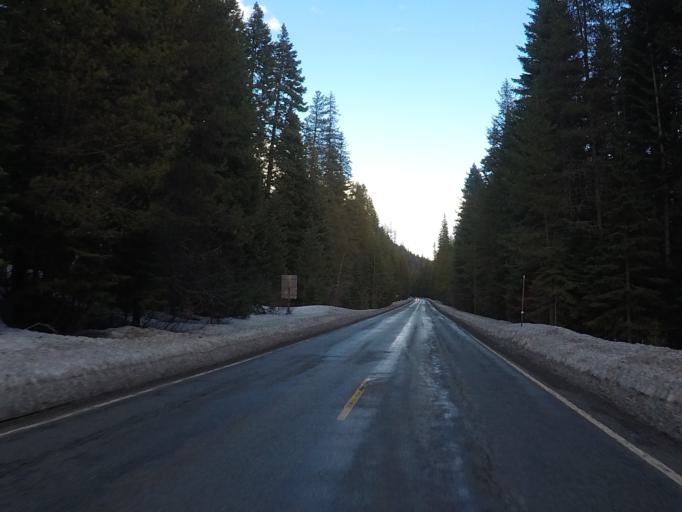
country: US
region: Montana
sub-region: Ravalli County
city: Hamilton
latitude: 46.5167
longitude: -114.7512
